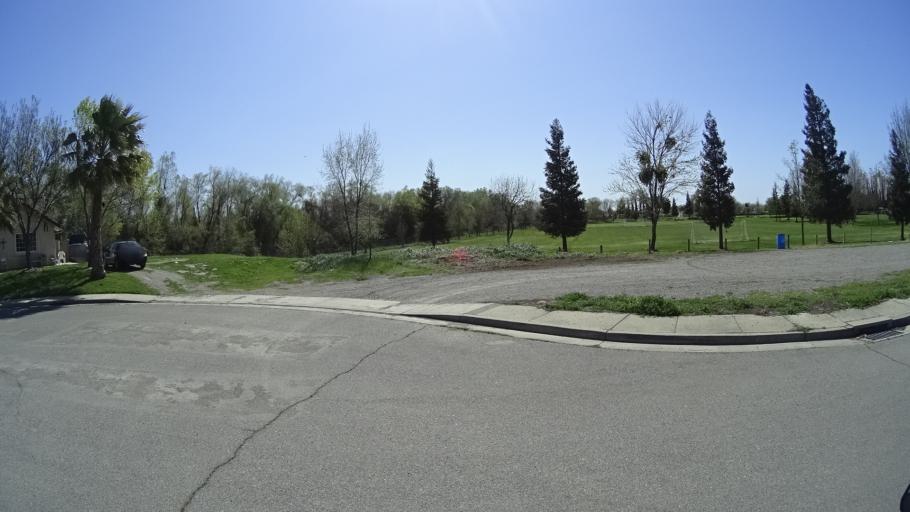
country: US
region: California
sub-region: Glenn County
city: Hamilton City
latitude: 39.7446
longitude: -122.0052
